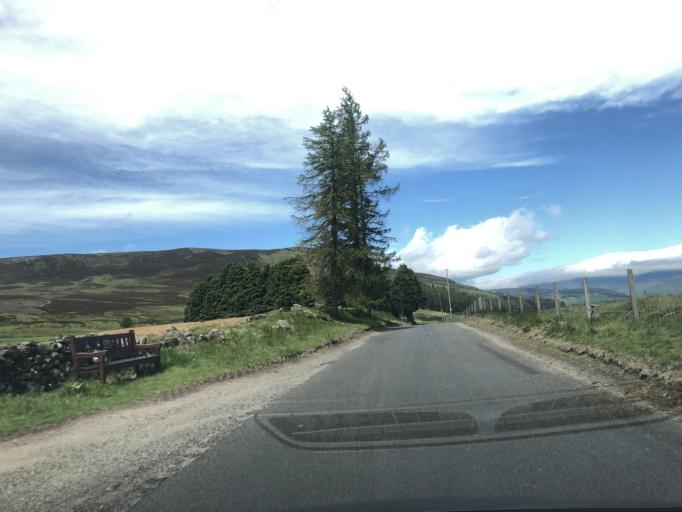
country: GB
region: Scotland
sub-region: Angus
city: Kirriemuir
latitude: 56.7673
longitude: -3.0222
